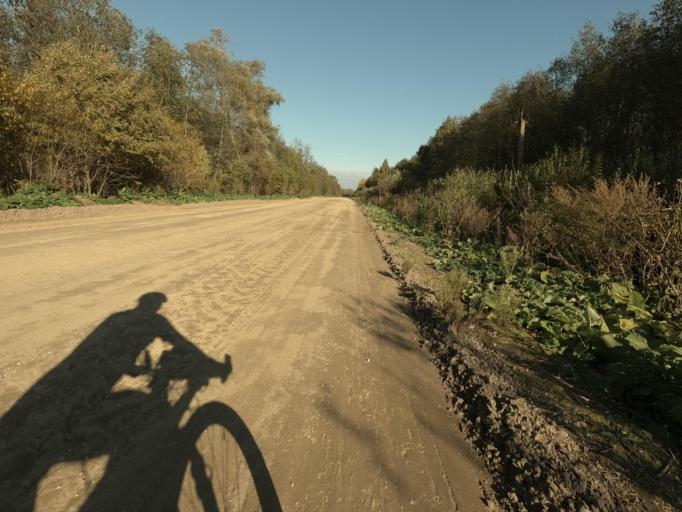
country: RU
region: Novgorod
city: Batetskiy
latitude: 58.8751
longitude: 30.7253
